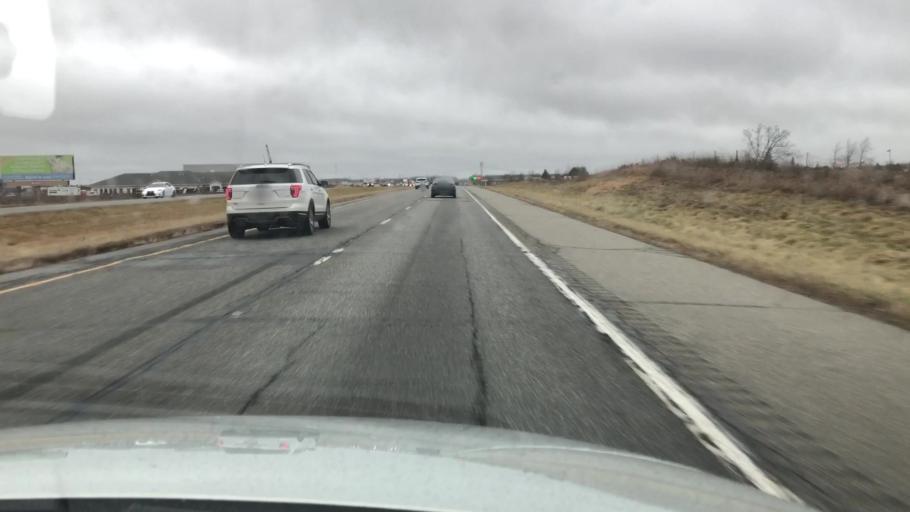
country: US
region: Indiana
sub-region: Marshall County
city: Plymouth
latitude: 41.3616
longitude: -86.3400
